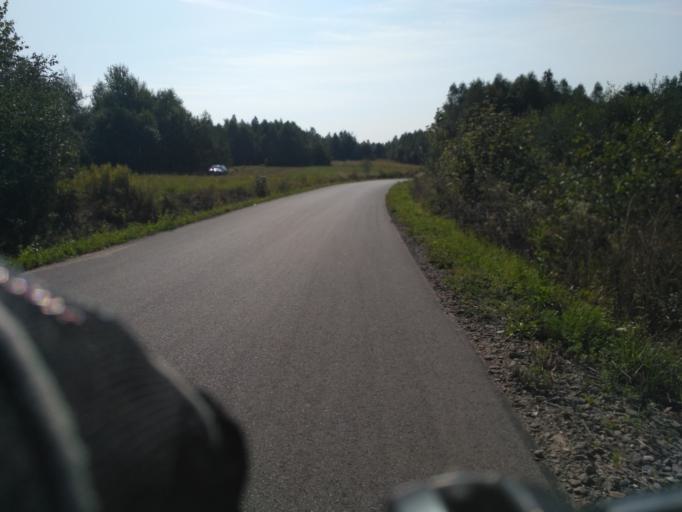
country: PL
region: Subcarpathian Voivodeship
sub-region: Powiat strzyzowski
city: Gwoznica Gorna
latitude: 49.8061
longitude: 22.0238
